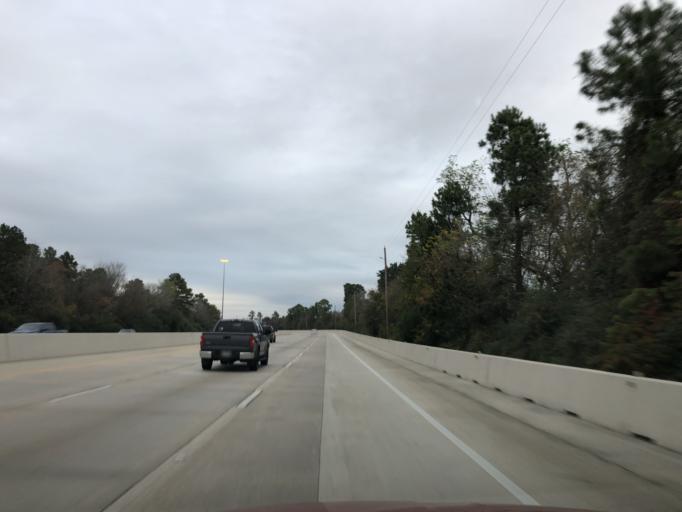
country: US
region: Texas
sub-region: Harris County
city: Spring
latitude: 30.0494
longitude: -95.4047
